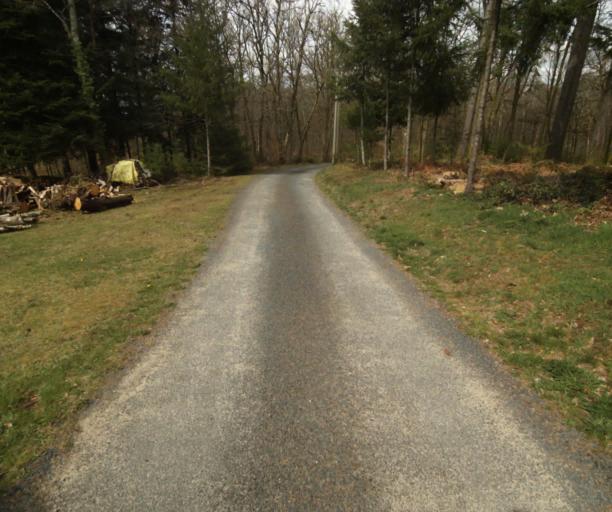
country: FR
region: Limousin
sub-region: Departement de la Correze
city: Argentat
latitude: 45.2223
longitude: 1.9224
